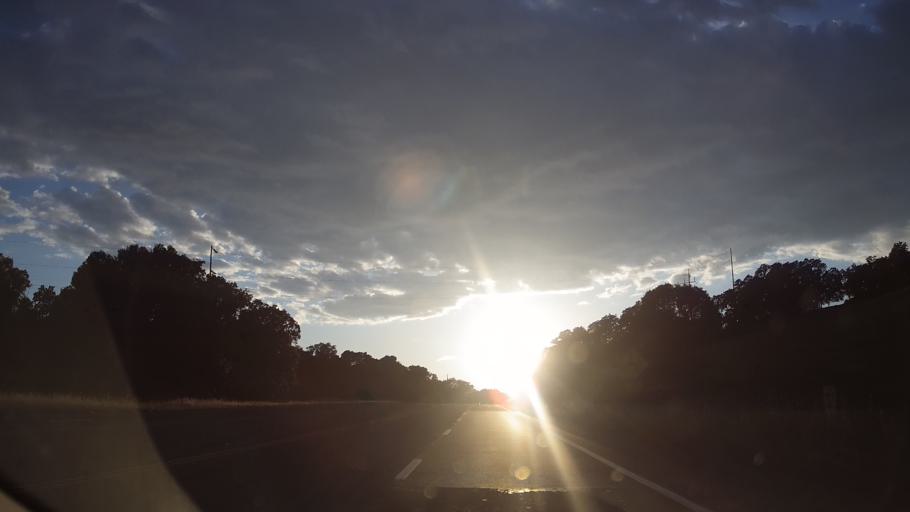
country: US
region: California
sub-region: Mendocino County
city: Redwood Valley
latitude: 39.2716
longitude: -123.2447
